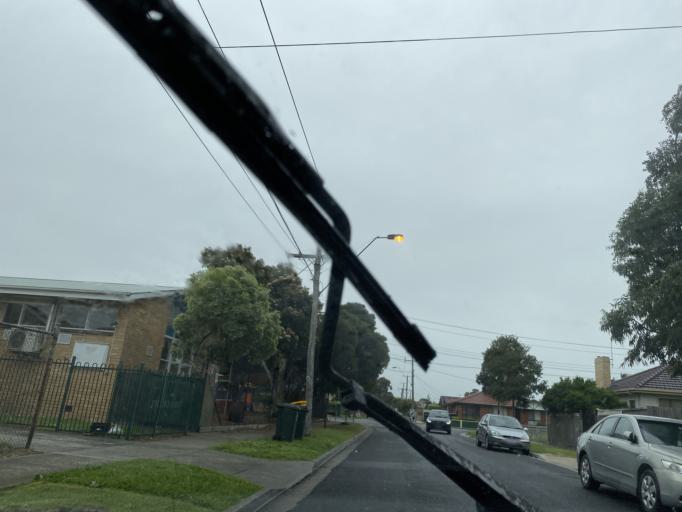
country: AU
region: Victoria
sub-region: Moreland
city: Fawkner
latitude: -37.7076
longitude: 144.9647
